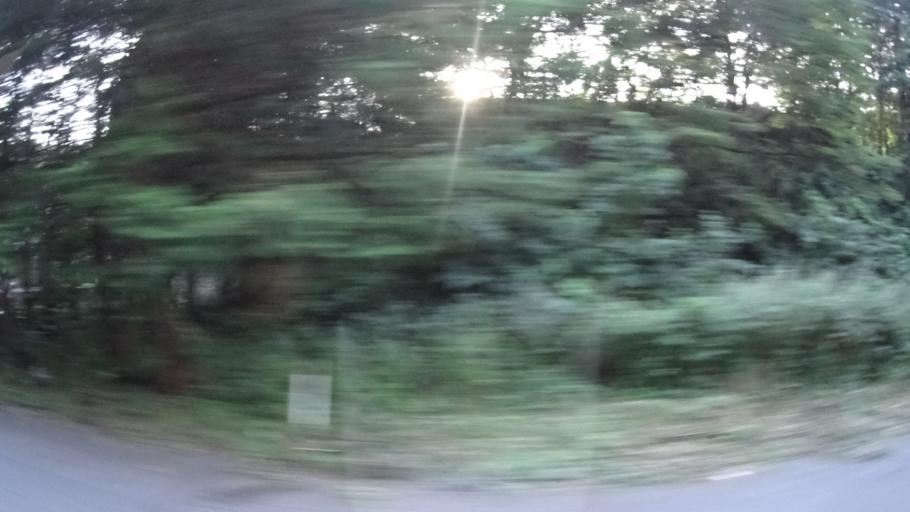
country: JP
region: Tochigi
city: Karasuyama
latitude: 36.6081
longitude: 140.1535
